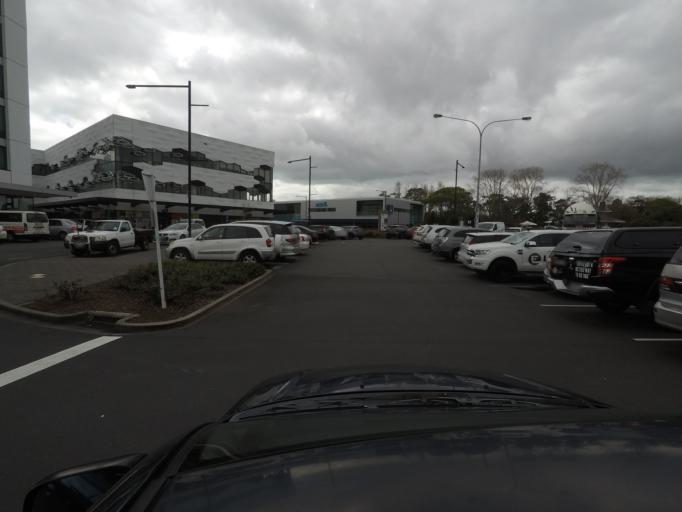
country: NZ
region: Auckland
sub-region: Auckland
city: Tamaki
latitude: -36.9378
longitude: 174.8749
